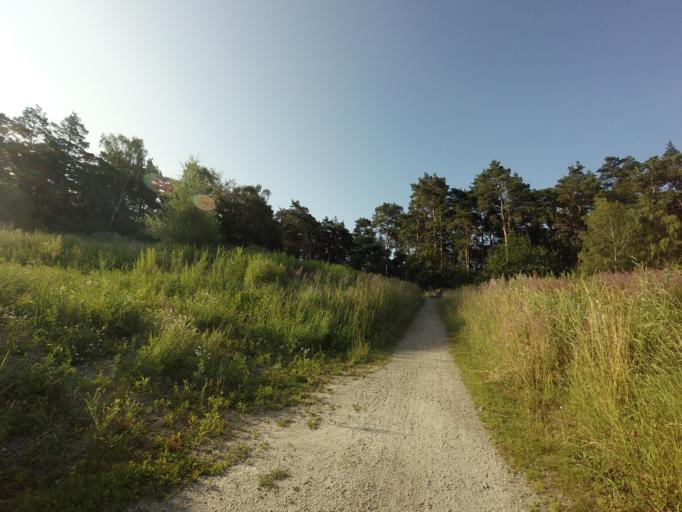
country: SE
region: Skane
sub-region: Landskrona
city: Asmundtorp
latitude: 55.8441
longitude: 12.9257
